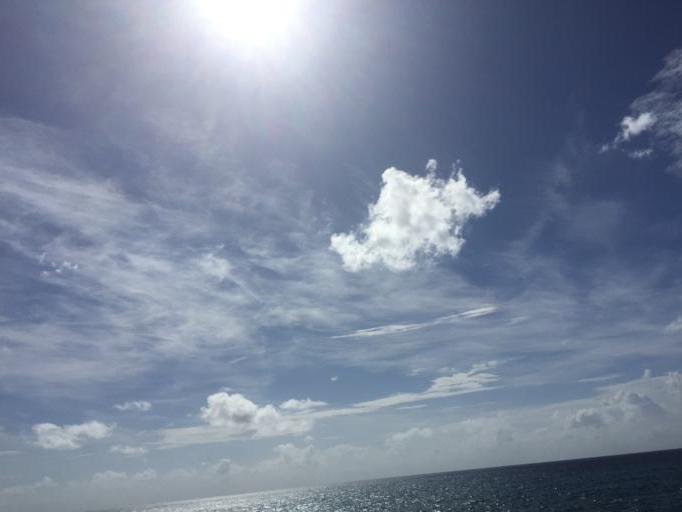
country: DO
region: Santo Domingo
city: Guerra
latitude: 18.4553
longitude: -69.7090
